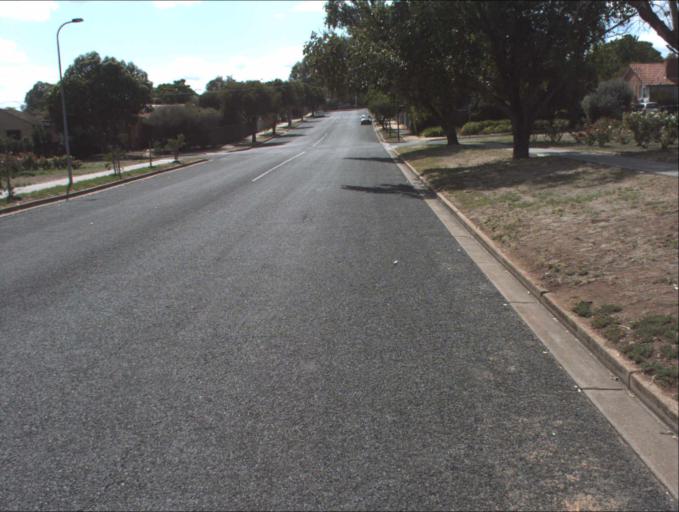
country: AU
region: South Australia
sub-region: Port Adelaide Enfield
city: Blair Athol
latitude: -34.8574
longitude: 138.5977
